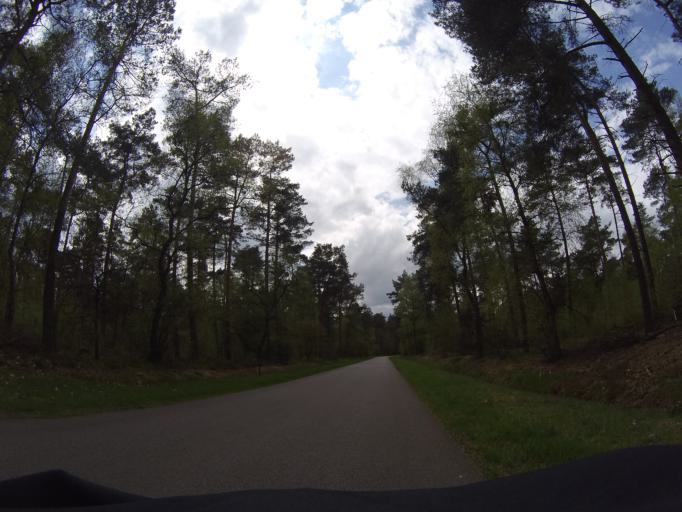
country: NL
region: Overijssel
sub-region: Gemeente Twenterand
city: Den Ham
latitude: 52.5147
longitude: 6.4796
